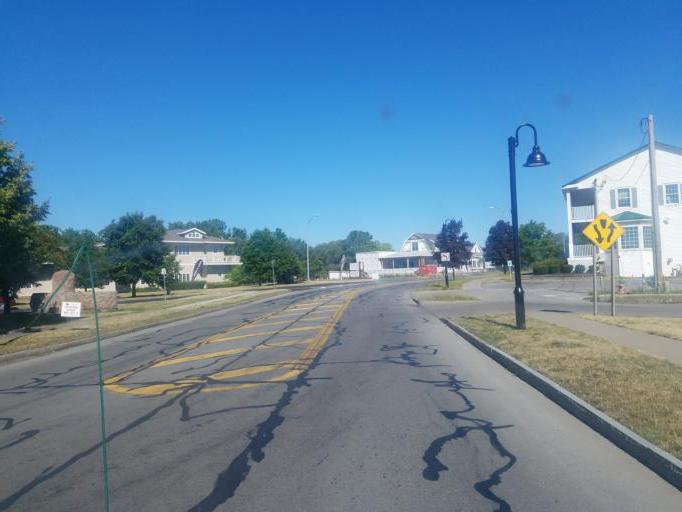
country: US
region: New York
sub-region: Ontario County
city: Canandaigua
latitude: 42.8761
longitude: -77.2723
